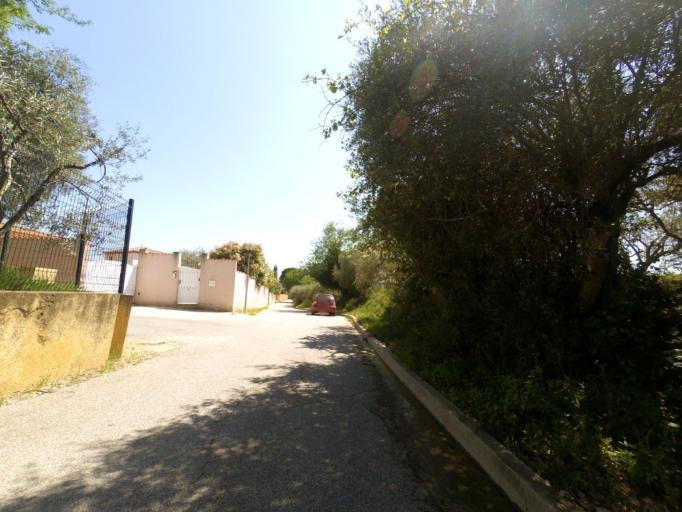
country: FR
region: Languedoc-Roussillon
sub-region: Departement du Gard
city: Calvisson
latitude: 43.7782
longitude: 4.1841
